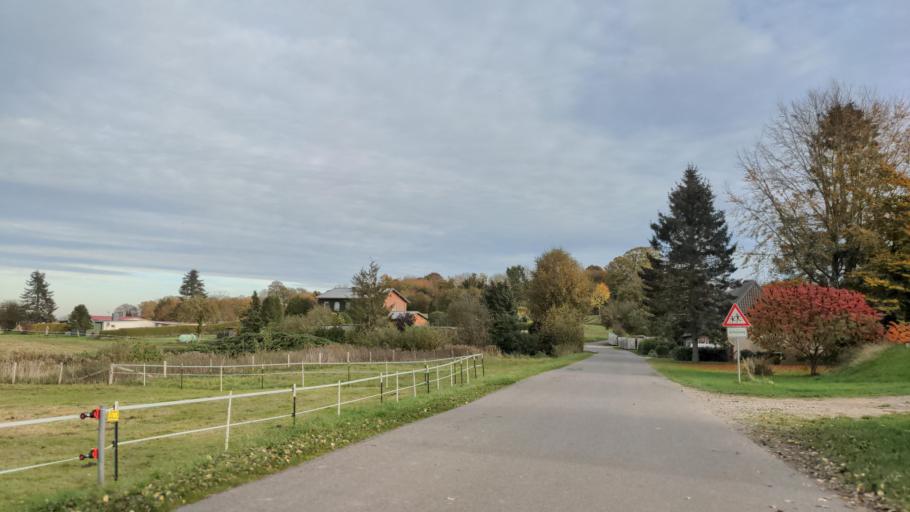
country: DE
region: Schleswig-Holstein
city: Malente
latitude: 54.1115
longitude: 10.5401
